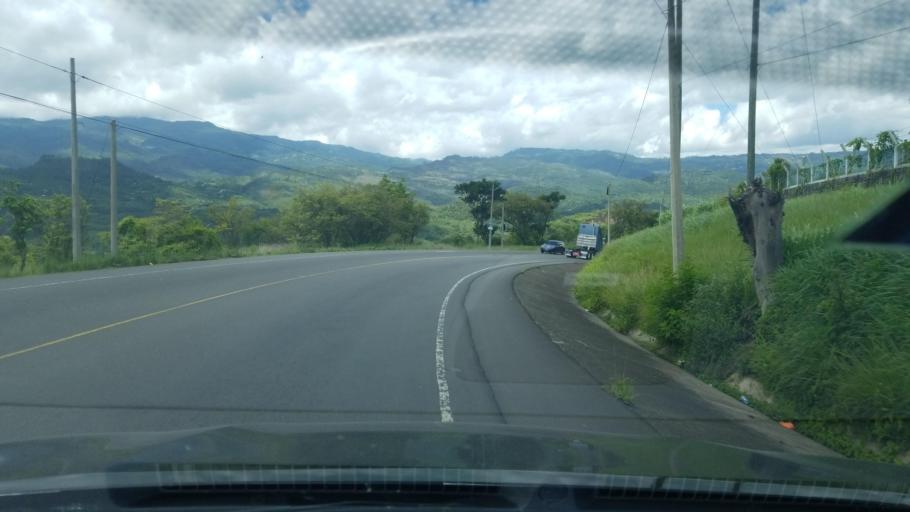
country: HN
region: Francisco Morazan
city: Cofradia
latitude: 14.2058
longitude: -87.2115
